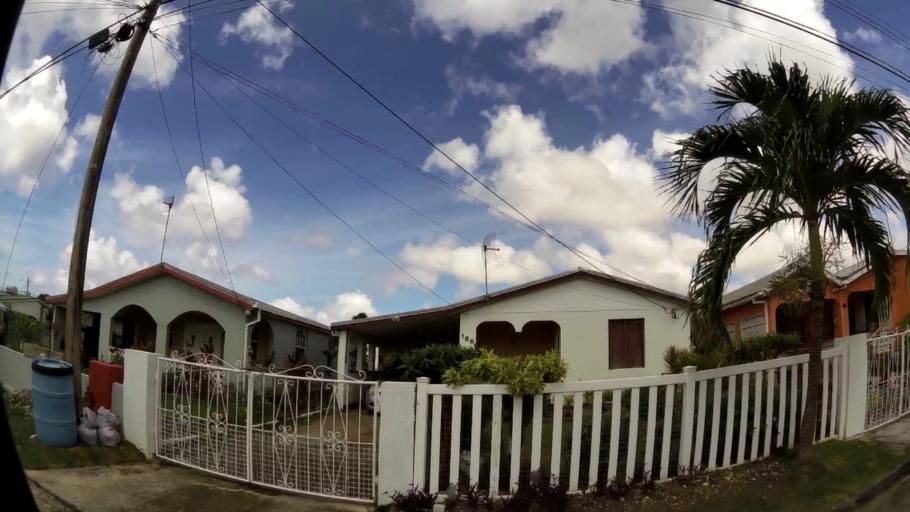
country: BB
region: Saint James
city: Holetown
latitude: 13.1511
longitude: -59.6285
